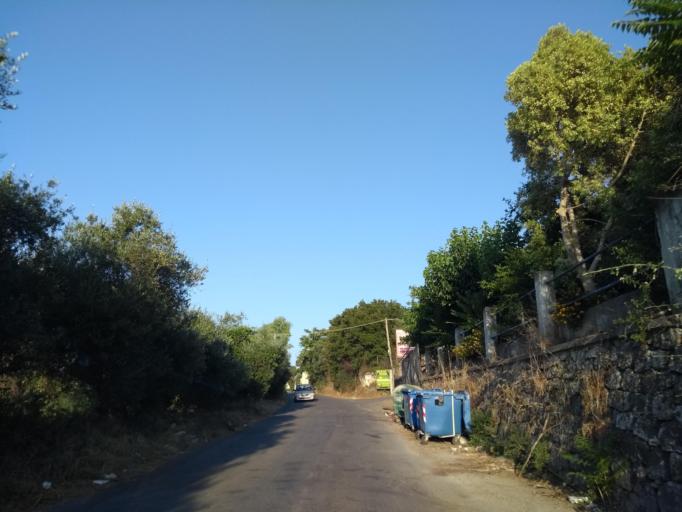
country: GR
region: Crete
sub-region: Nomos Chanias
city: Kalivai
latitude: 35.4076
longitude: 24.2003
